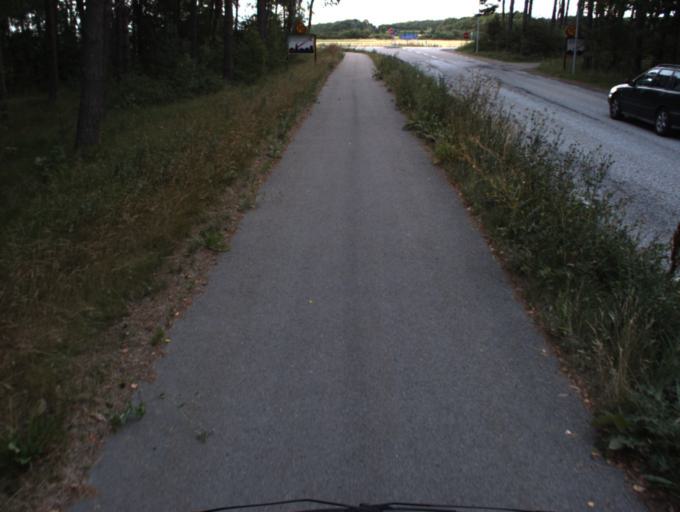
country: DK
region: Capital Region
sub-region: Helsingor Kommune
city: Hellebaek
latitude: 56.1255
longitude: 12.6011
